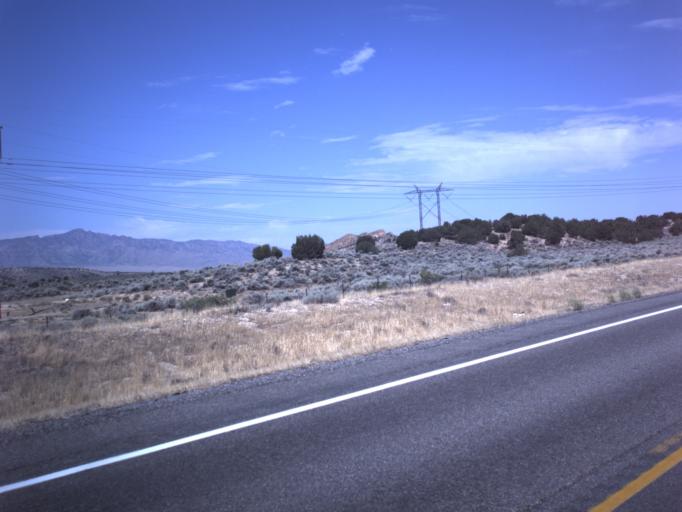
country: US
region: Utah
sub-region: Sanpete County
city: Gunnison
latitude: 39.3503
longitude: -111.9285
